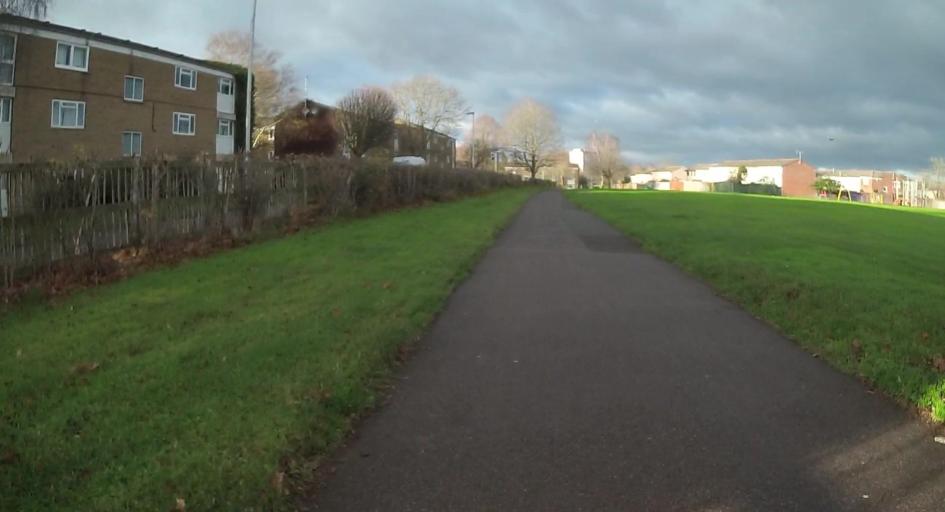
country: GB
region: England
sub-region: Bracknell Forest
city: Bracknell
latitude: 51.4009
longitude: -0.7703
